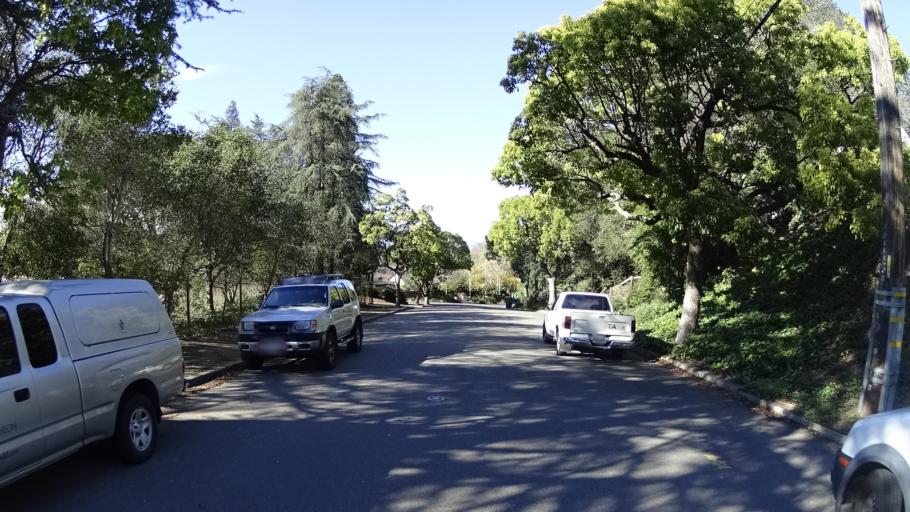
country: US
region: California
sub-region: Alameda County
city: Piedmont
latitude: 37.8299
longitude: -122.2173
